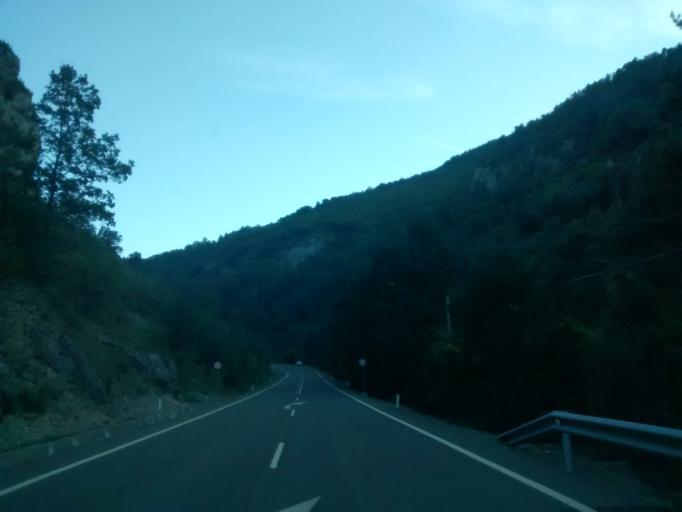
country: ES
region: Aragon
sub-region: Provincia de Huesca
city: Aragues del Puerto
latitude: 42.7012
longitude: -0.7470
